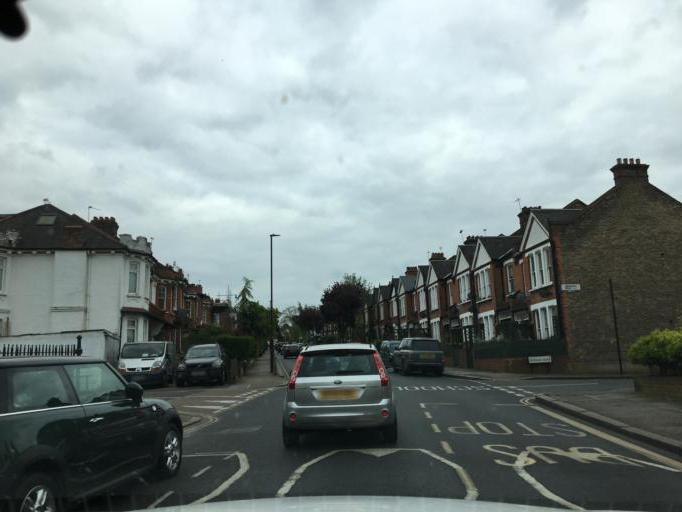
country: GB
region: England
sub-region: Greater London
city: Brixton
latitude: 51.4627
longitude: -0.0981
